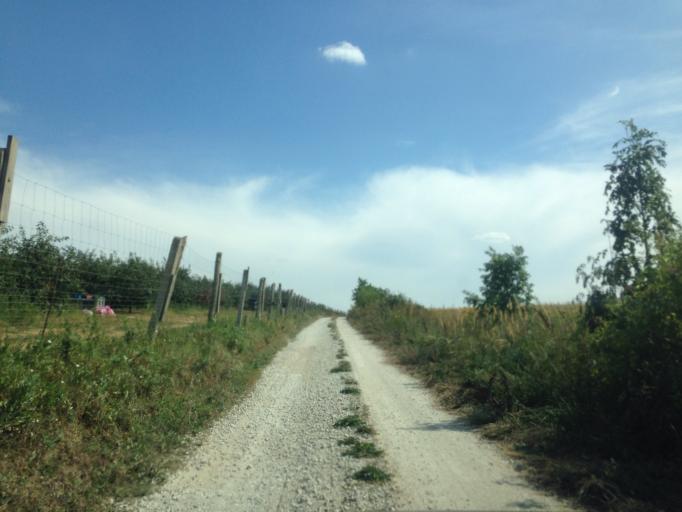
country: PL
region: Kujawsko-Pomorskie
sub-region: Powiat brodnicki
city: Bartniczka
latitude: 53.2352
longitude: 19.5792
